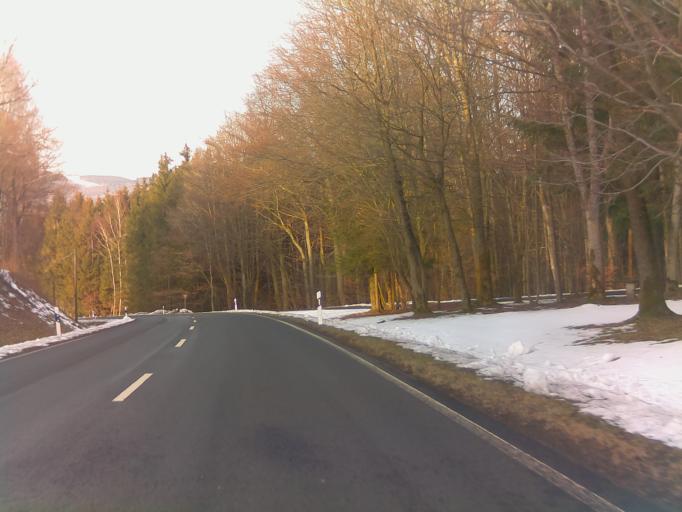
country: DE
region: Bavaria
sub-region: Regierungsbezirk Unterfranken
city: Wildflecken
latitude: 50.3690
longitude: 9.9208
